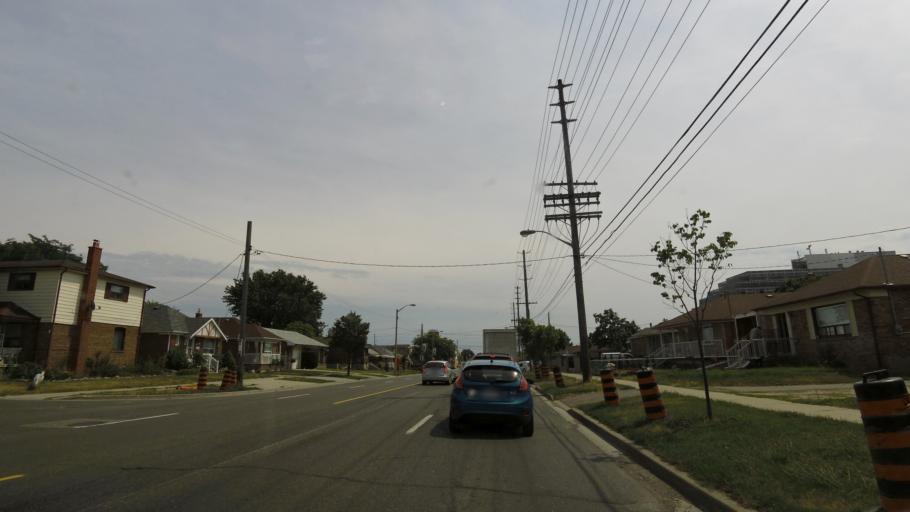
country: CA
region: Ontario
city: Etobicoke
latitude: 43.6254
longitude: -79.5156
